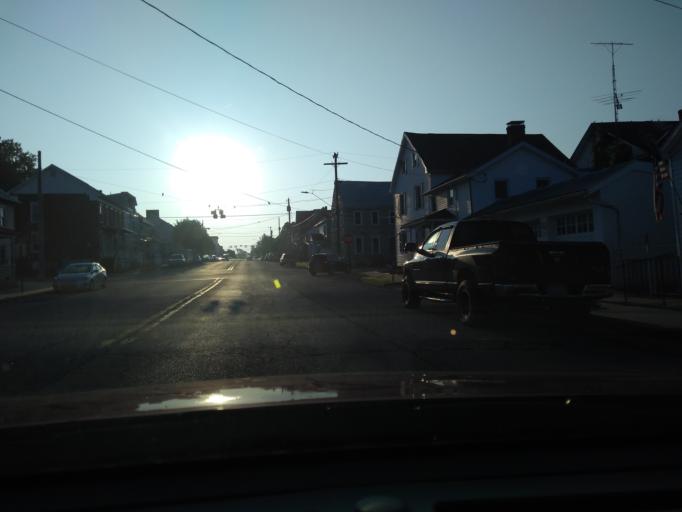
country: US
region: Maryland
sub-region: Washington County
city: Williamsport
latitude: 39.5991
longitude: -77.8242
